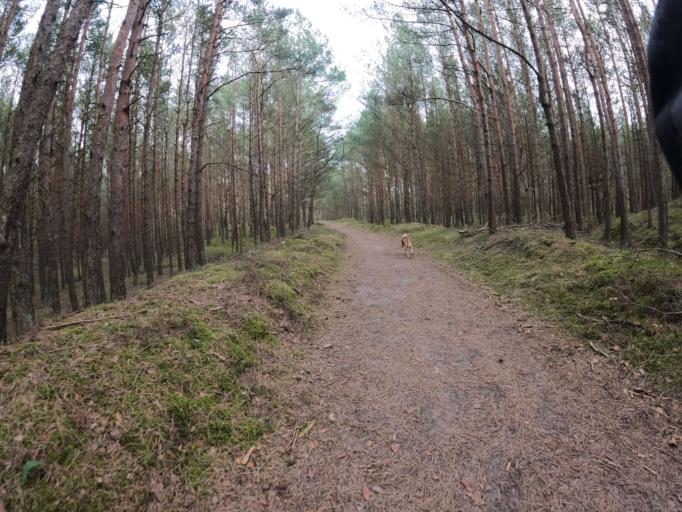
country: PL
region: West Pomeranian Voivodeship
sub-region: Powiat gryficki
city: Mrzezyno
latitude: 54.1348
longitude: 15.2503
